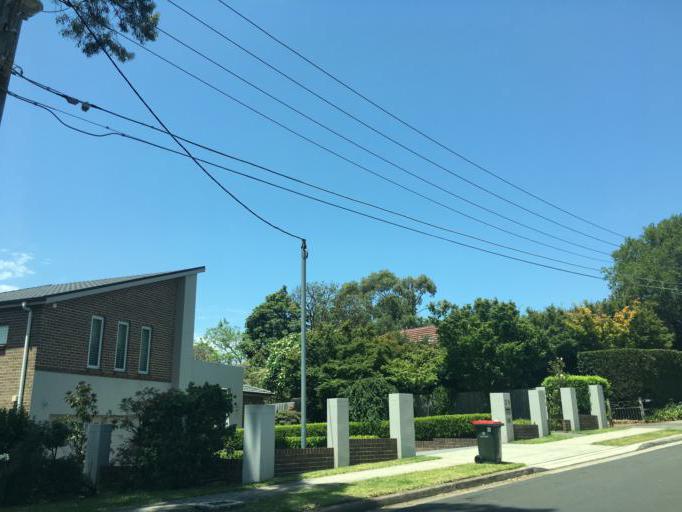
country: AU
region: New South Wales
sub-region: Ryde
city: Denistone
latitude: -33.8005
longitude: 151.1060
